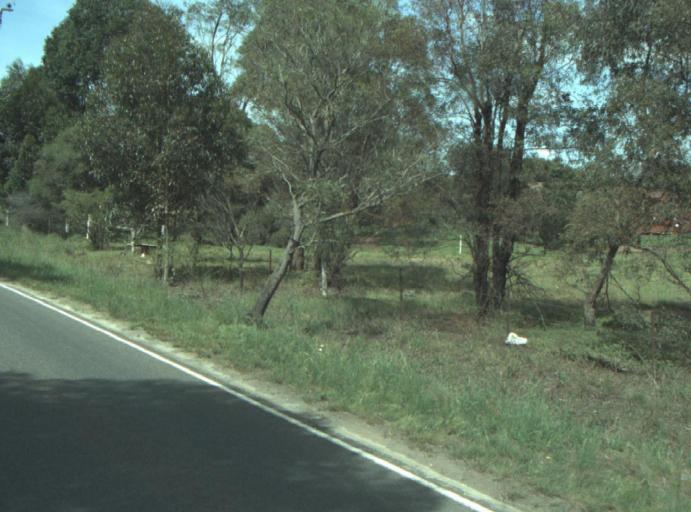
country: AU
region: Victoria
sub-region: Greater Geelong
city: Lara
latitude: -38.0404
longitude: 144.4304
